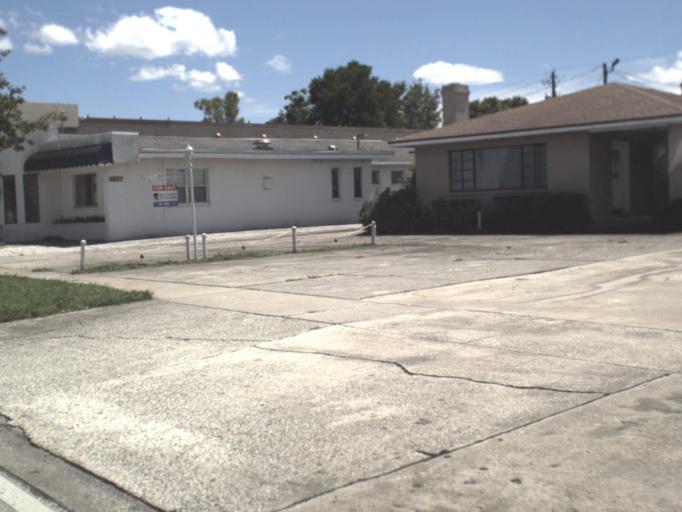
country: US
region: Florida
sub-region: Polk County
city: Lakeland
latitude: 28.0528
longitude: -81.9341
